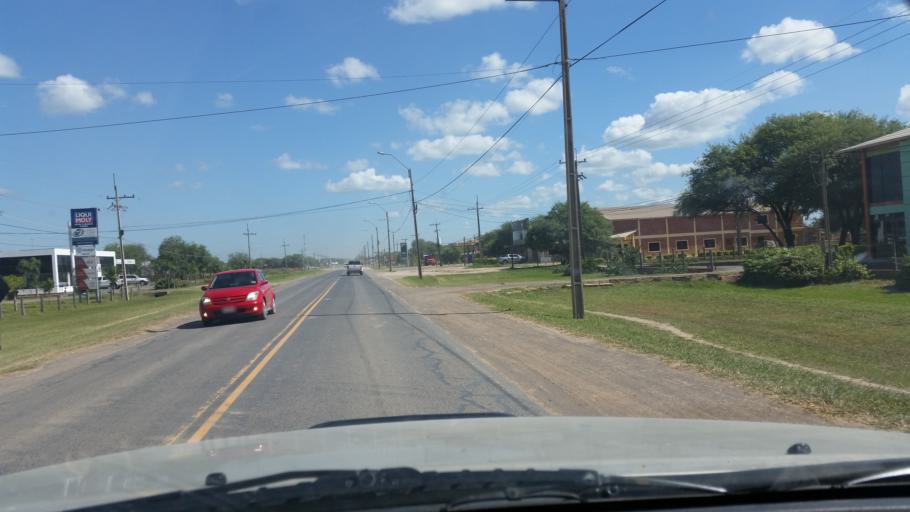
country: PY
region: Boqueron
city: Colonia Menno
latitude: -22.3964
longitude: -59.8365
